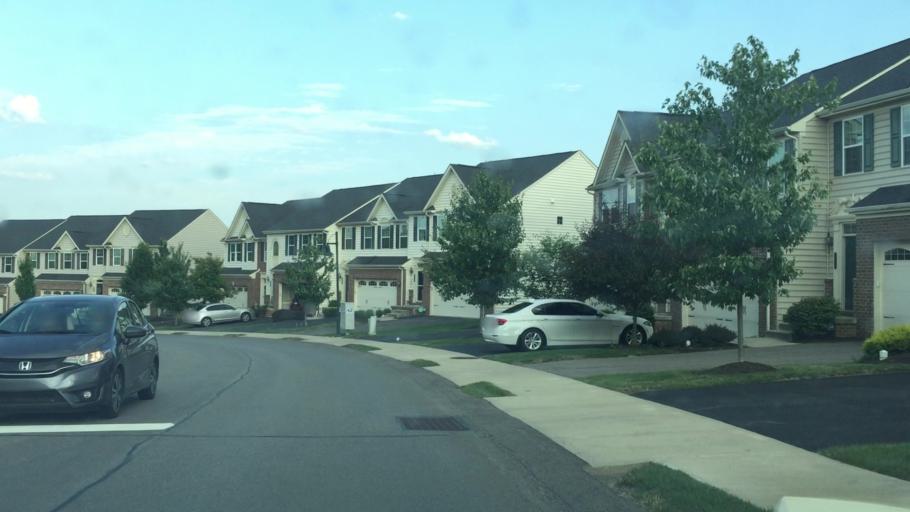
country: US
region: Pennsylvania
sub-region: Allegheny County
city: Bradford Woods
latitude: 40.6287
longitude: -80.0499
